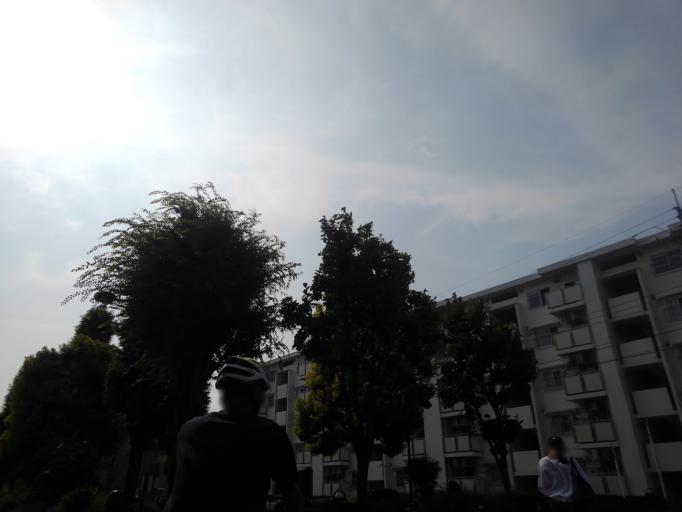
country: JP
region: Kanagawa
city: Minami-rinkan
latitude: 35.4703
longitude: 139.4580
